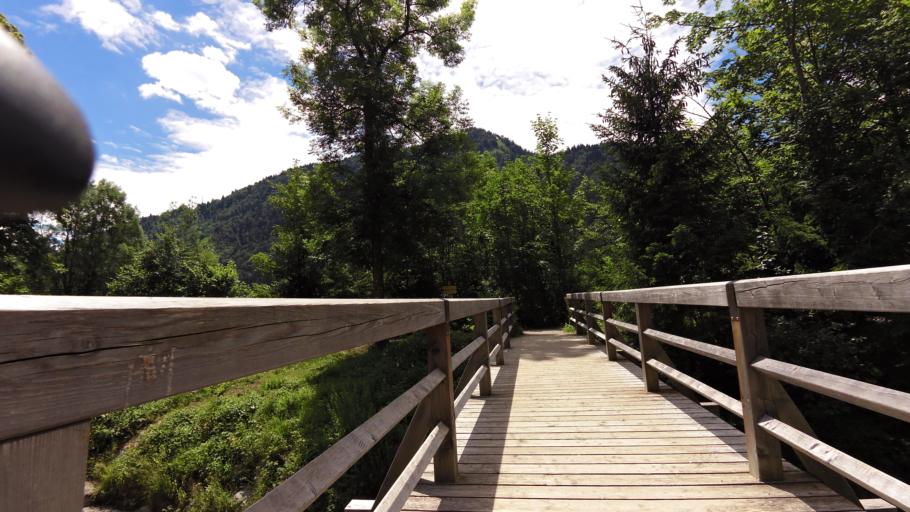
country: DE
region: Bavaria
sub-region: Upper Bavaria
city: Tegernsee
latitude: 47.6946
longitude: 11.7425
